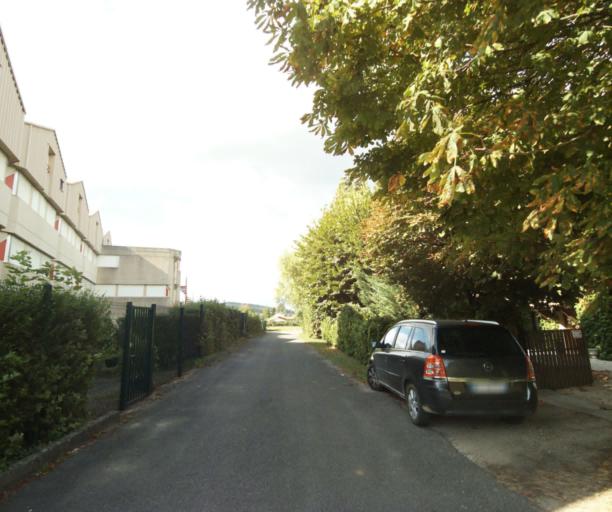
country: FR
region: Bourgogne
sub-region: Departement de Saone-et-Loire
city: Tournus
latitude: 46.5746
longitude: 4.9072
